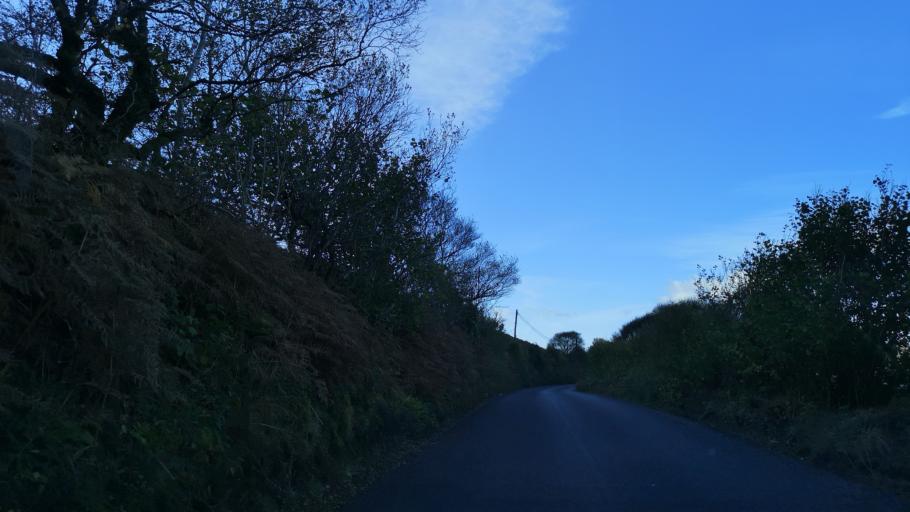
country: IE
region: Connaught
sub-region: County Galway
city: Clifden
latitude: 53.5037
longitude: -10.0687
